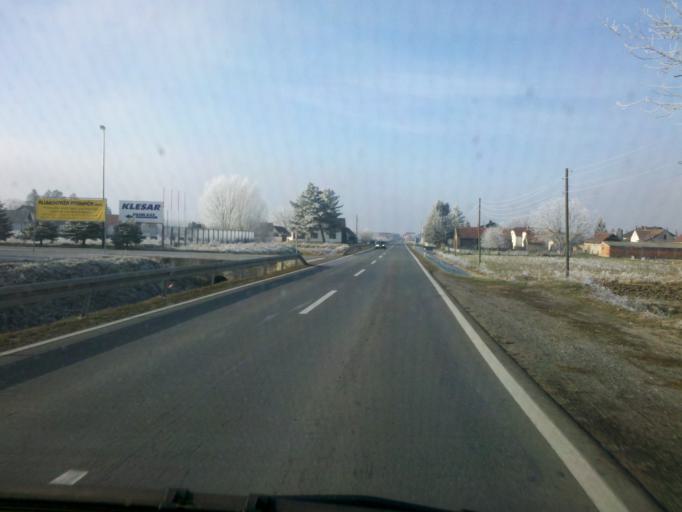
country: HR
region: Virovitick-Podravska
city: Pitomaca
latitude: 45.9664
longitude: 17.2051
